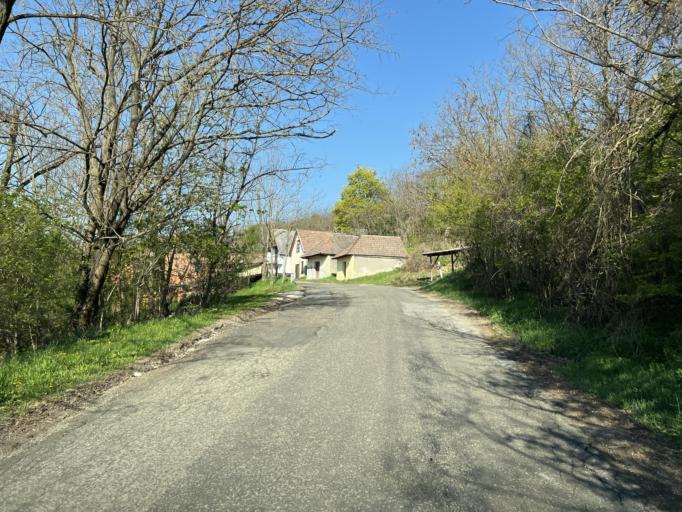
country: SK
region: Nitriansky
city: Sahy
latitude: 47.9987
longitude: 18.8577
